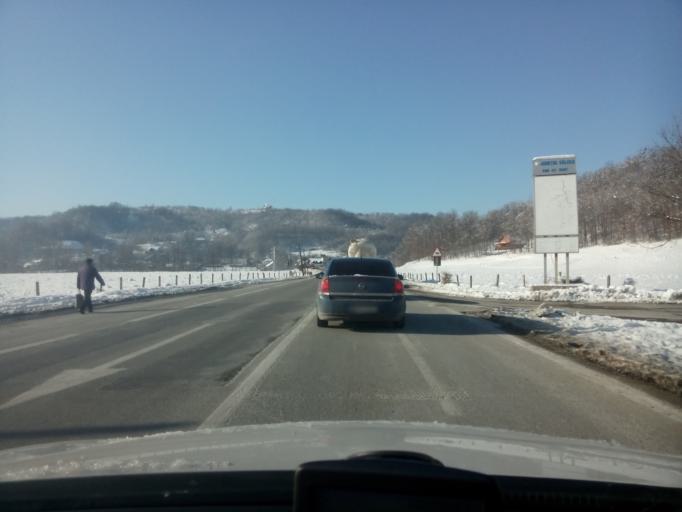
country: RO
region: Valcea
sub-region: Comuna Milcoiu
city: Milcoiu
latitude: 45.0257
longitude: 24.4887
